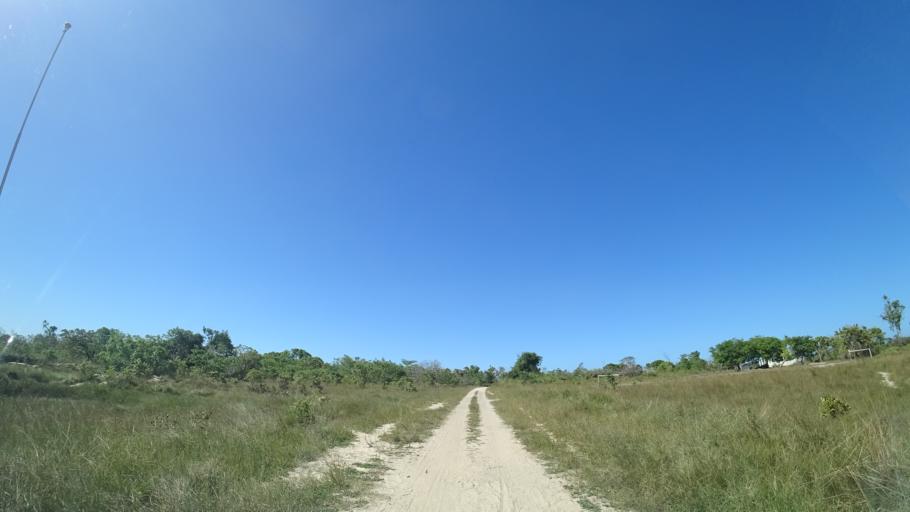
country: MZ
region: Sofala
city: Beira
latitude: -19.5742
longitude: 35.2251
